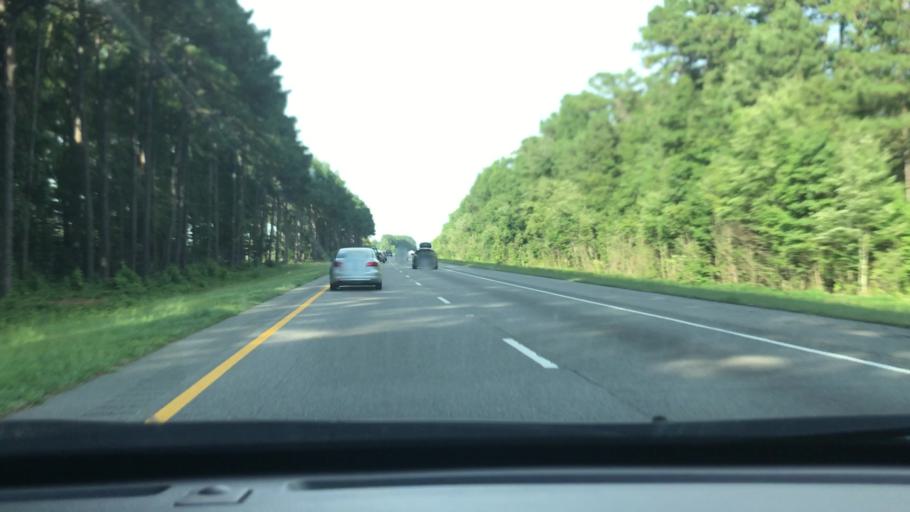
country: US
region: North Carolina
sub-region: Robeson County
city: Fairmont
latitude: 34.5828
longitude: -79.1387
